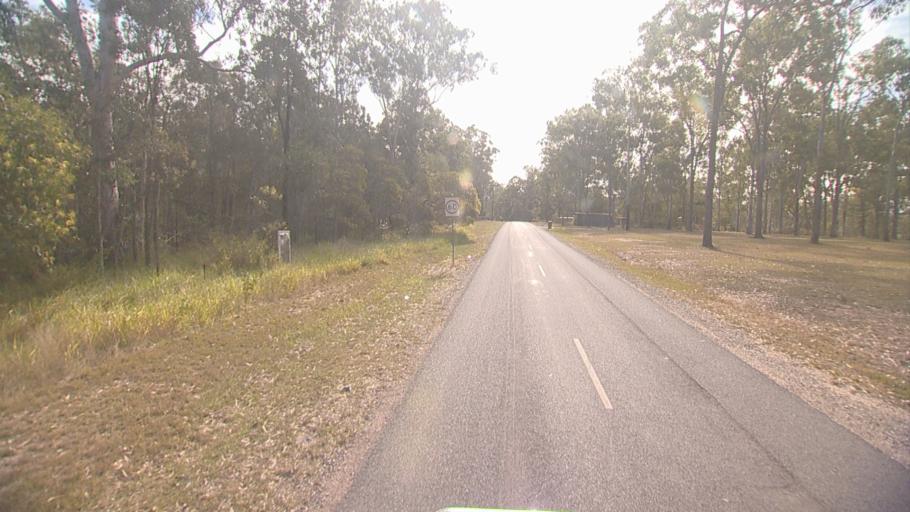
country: AU
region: Queensland
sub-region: Logan
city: North Maclean
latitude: -27.7490
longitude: 152.9736
